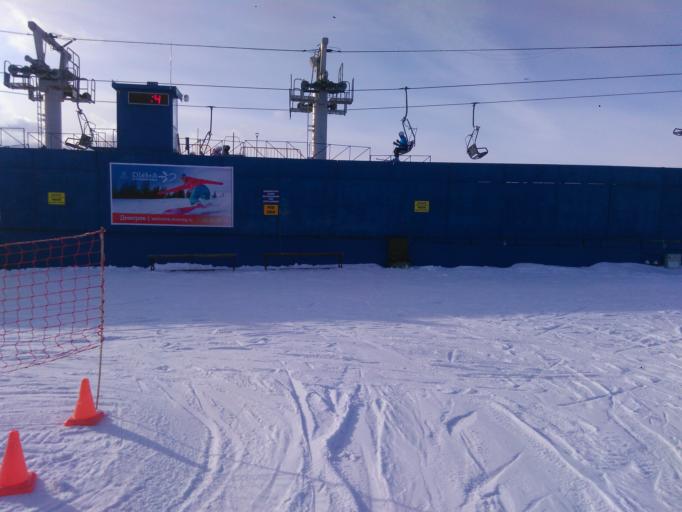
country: RU
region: Moskovskaya
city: Dedenevo
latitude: 56.2756
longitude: 37.5633
